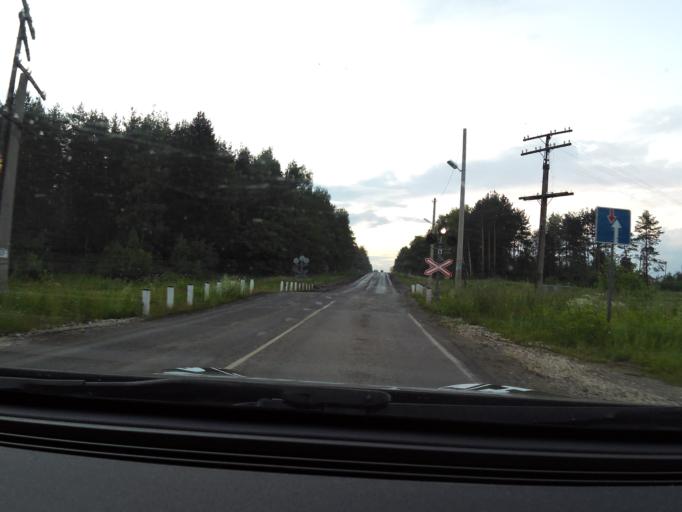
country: RU
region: Vladimir
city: Kol'chugino
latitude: 56.2860
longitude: 39.3331
